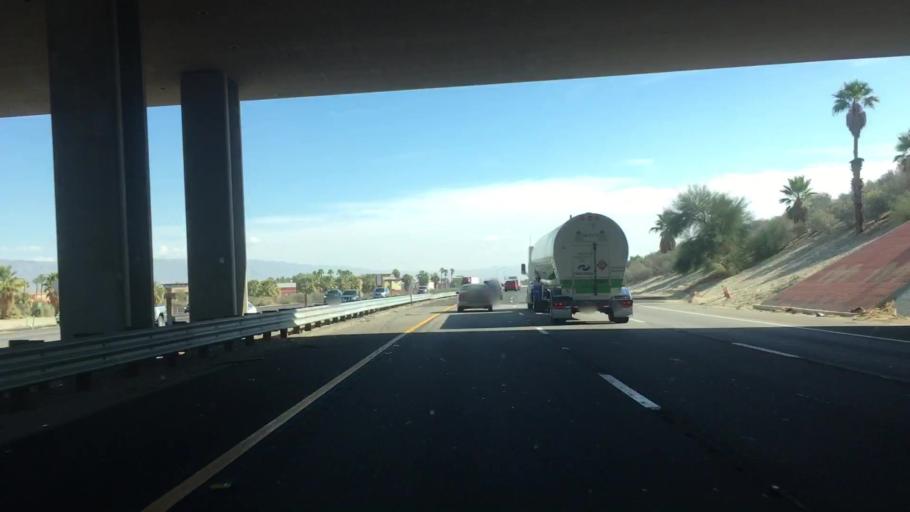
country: US
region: California
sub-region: Riverside County
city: Bermuda Dunes
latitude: 33.7604
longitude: -116.3013
